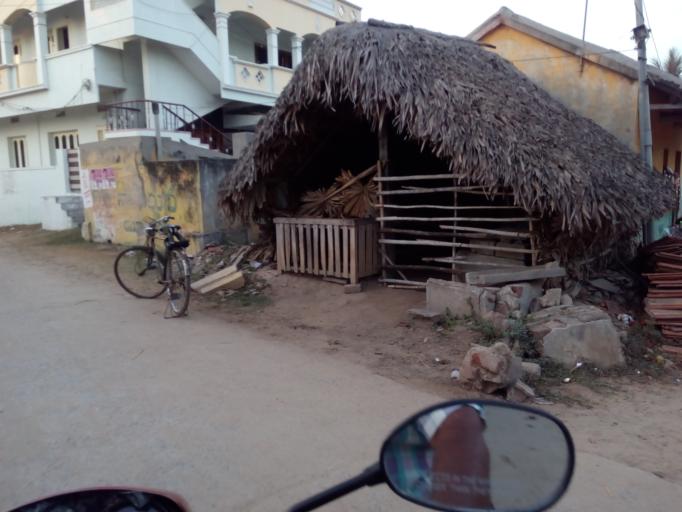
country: IN
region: Andhra Pradesh
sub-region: Prakasam
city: Vetapalem
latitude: 15.7274
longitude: 80.2531
